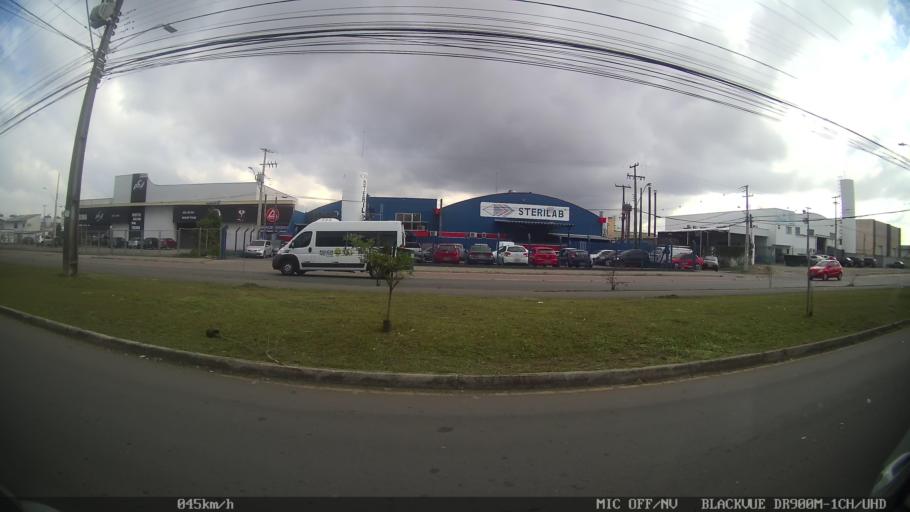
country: BR
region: Parana
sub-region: Pinhais
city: Pinhais
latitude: -25.4302
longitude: -49.1929
